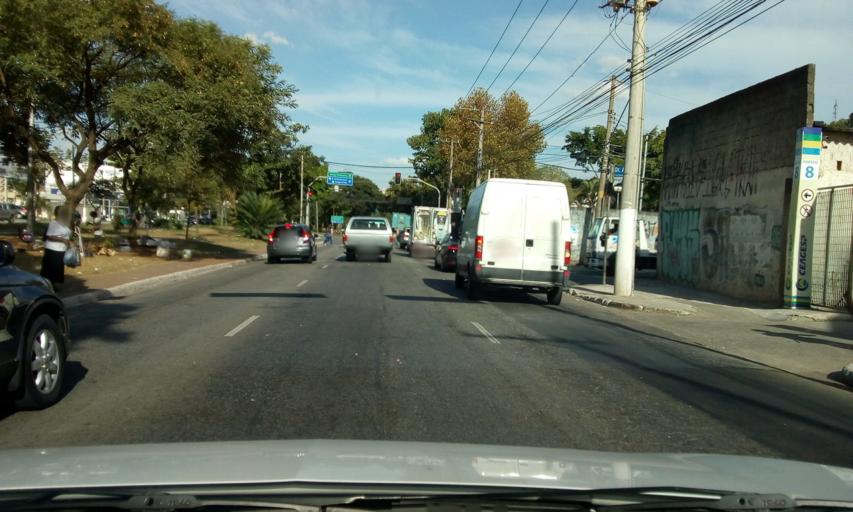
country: BR
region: Sao Paulo
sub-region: Osasco
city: Osasco
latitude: -23.5379
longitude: -46.7313
